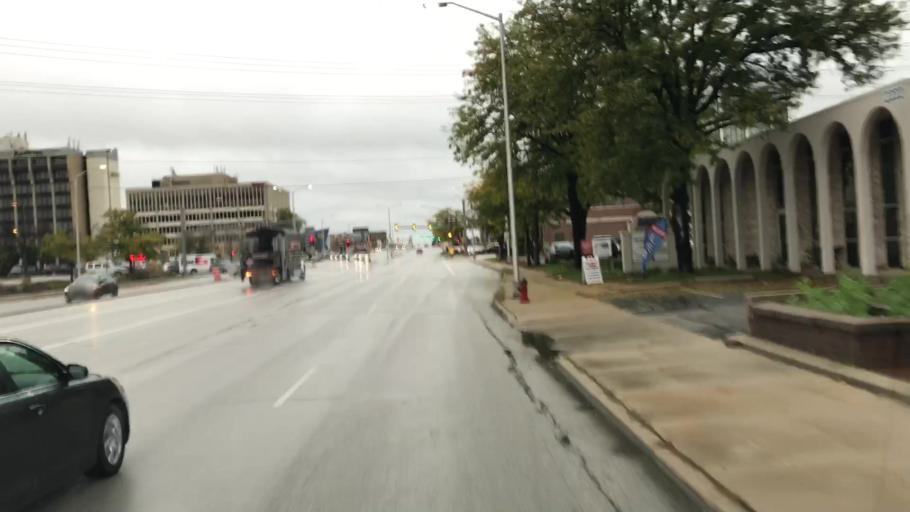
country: US
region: Wisconsin
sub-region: Waukesha County
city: Elm Grove
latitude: 43.0586
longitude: -88.0475
